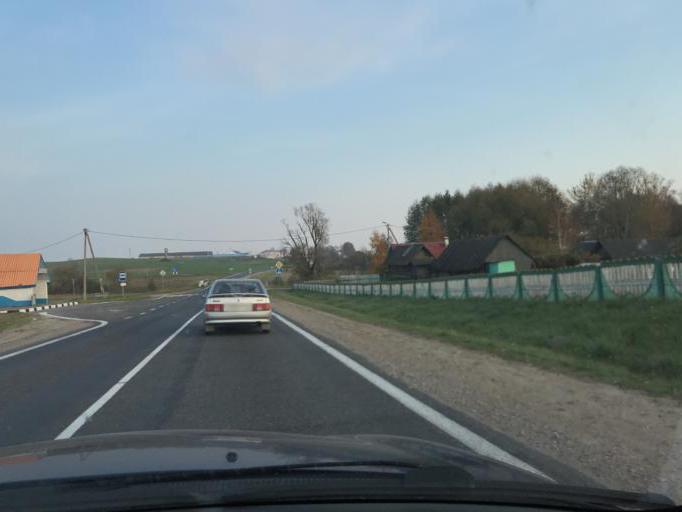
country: BY
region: Grodnenskaya
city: Karelichy
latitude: 53.5896
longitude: 26.0982
